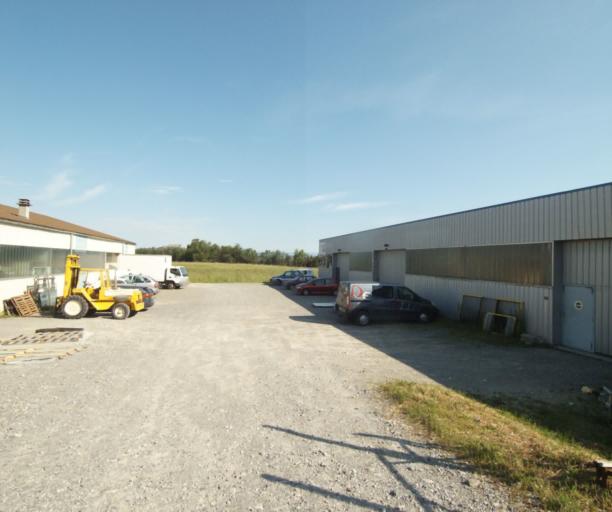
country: FR
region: Rhone-Alpes
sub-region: Departement de la Haute-Savoie
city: Allinges
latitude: 46.3154
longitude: 6.4850
